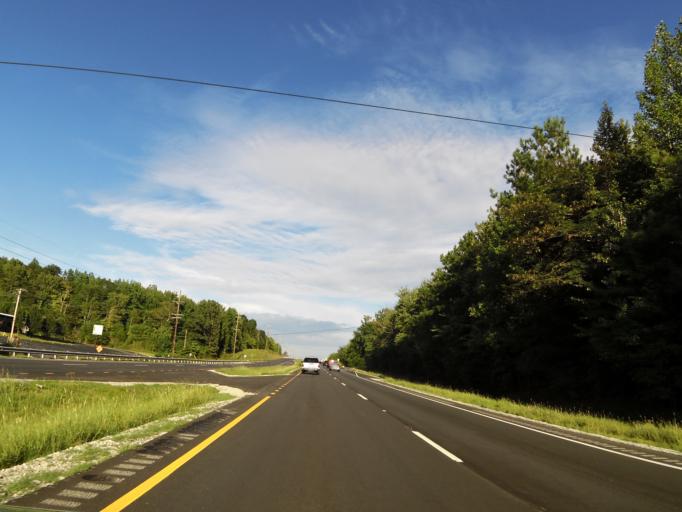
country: US
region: Alabama
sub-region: Lauderdale County
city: Killen
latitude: 34.8596
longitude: -87.5079
